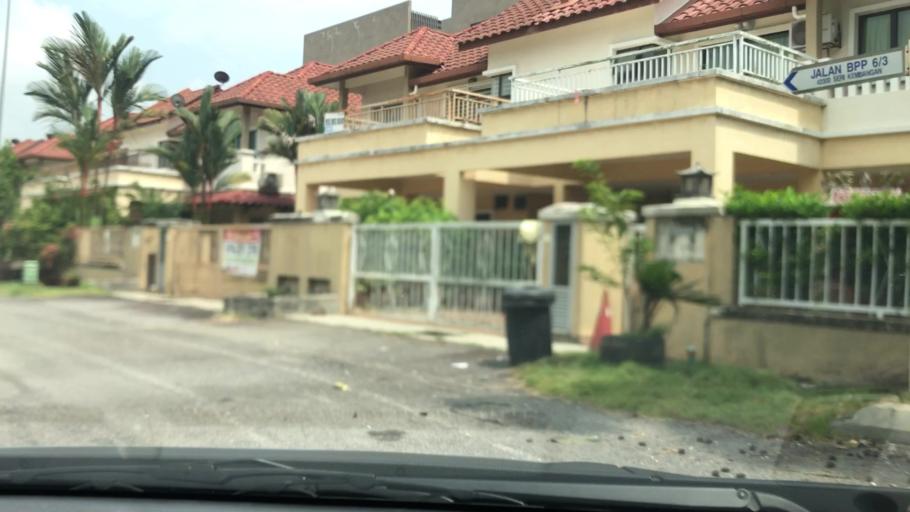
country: MY
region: Putrajaya
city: Putrajaya
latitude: 2.9890
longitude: 101.6682
